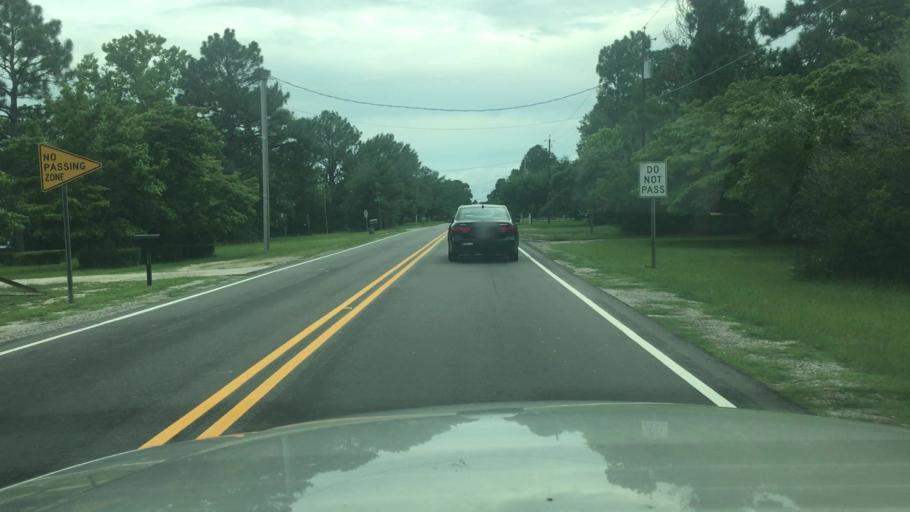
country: US
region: North Carolina
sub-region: Cumberland County
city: Hope Mills
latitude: 34.9721
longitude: -78.9605
